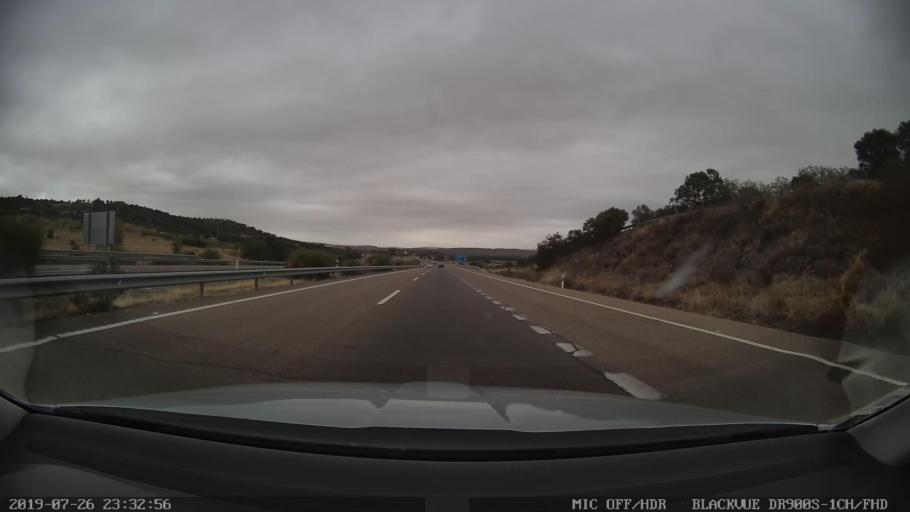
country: ES
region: Extremadura
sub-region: Provincia de Caceres
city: Puerto de Santa Cruz
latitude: 39.3293
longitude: -5.8573
